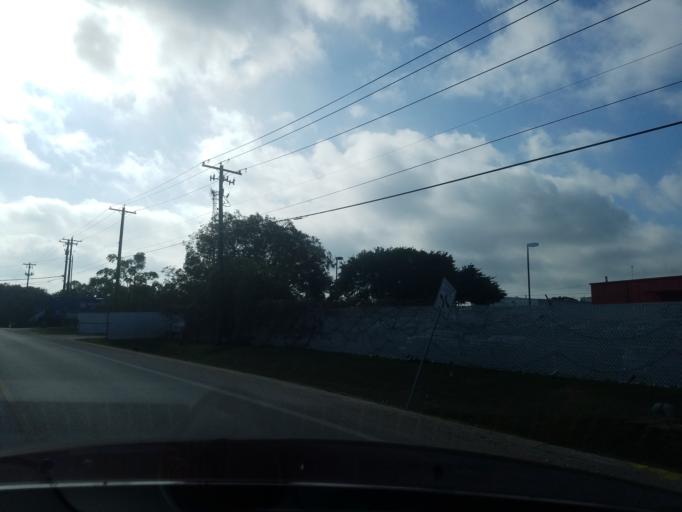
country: US
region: Texas
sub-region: Williamson County
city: Anderson Mill
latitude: 30.4531
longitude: -97.7890
